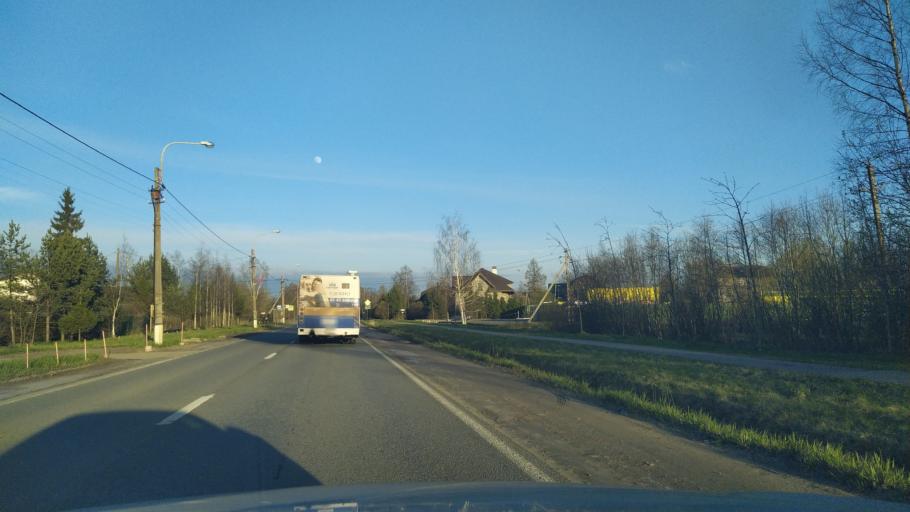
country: RU
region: St.-Petersburg
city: Aleksandrovskaya
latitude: 59.7368
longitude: 30.3313
